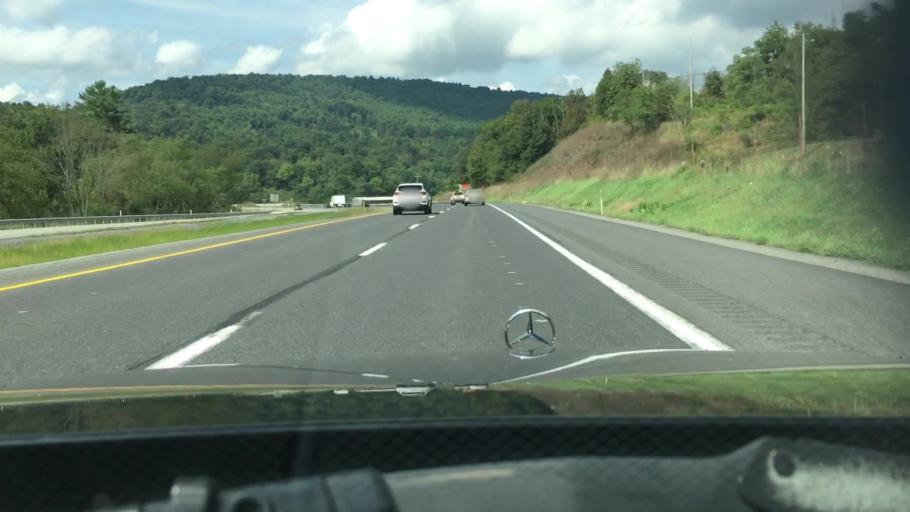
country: US
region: Pennsylvania
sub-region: Bedford County
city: Earlston
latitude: 39.9457
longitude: -78.2282
